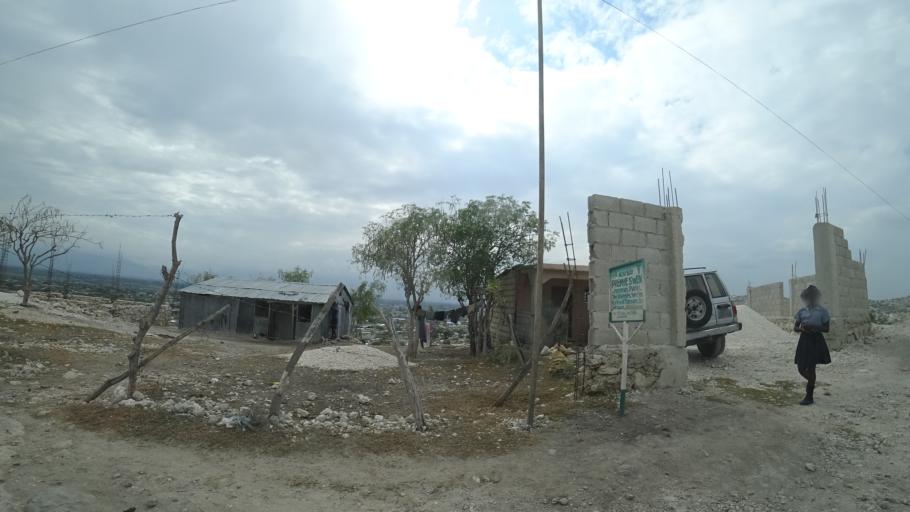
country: HT
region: Ouest
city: Croix des Bouquets
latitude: 18.6628
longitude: -72.2577
